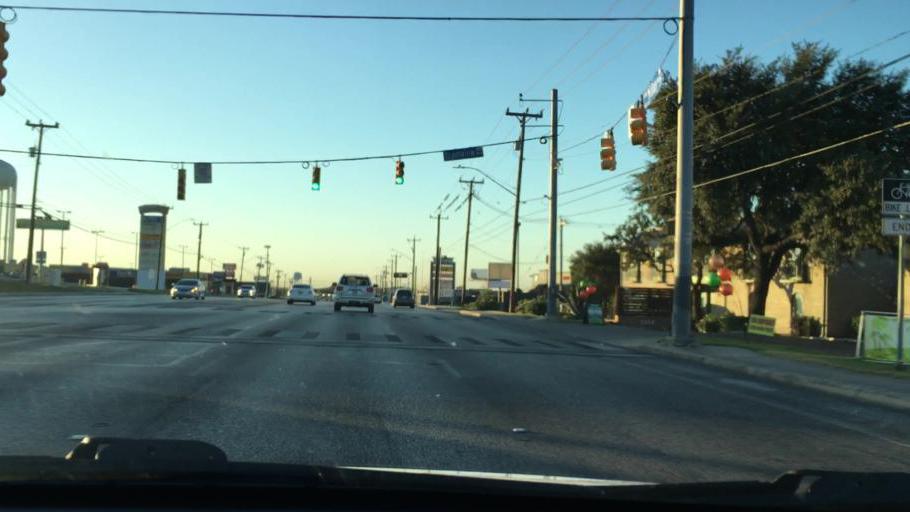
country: US
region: Texas
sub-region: Bexar County
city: Castle Hills
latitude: 29.5451
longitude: -98.5296
